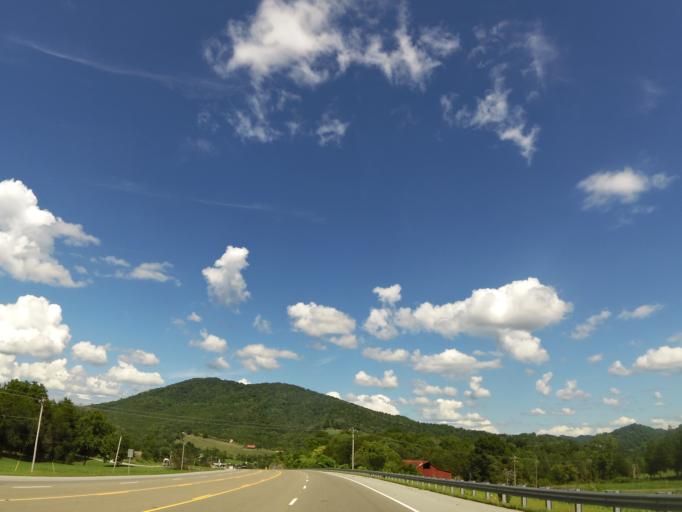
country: US
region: Tennessee
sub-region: Claiborne County
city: Tazewell
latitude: 36.4221
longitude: -83.5332
